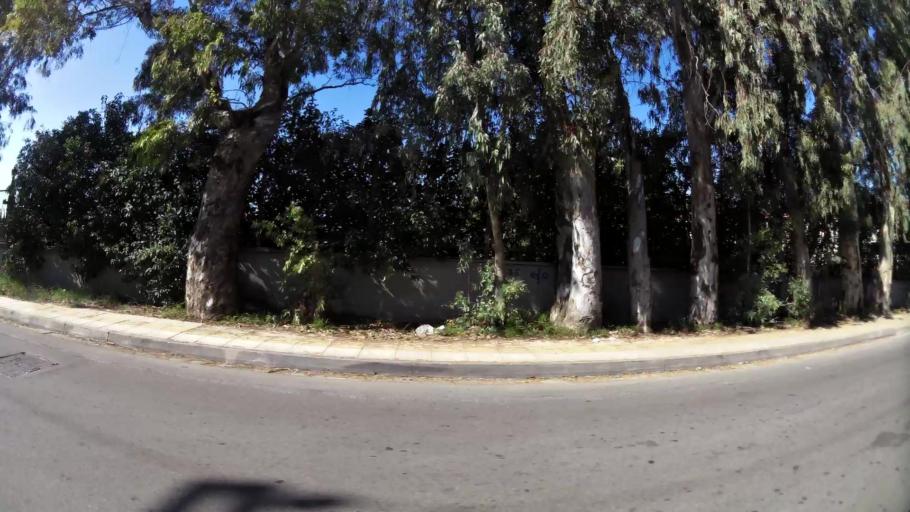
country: GR
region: Attica
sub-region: Nomarchia Athinas
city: Lykovrysi
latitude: 38.0754
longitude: 23.7940
